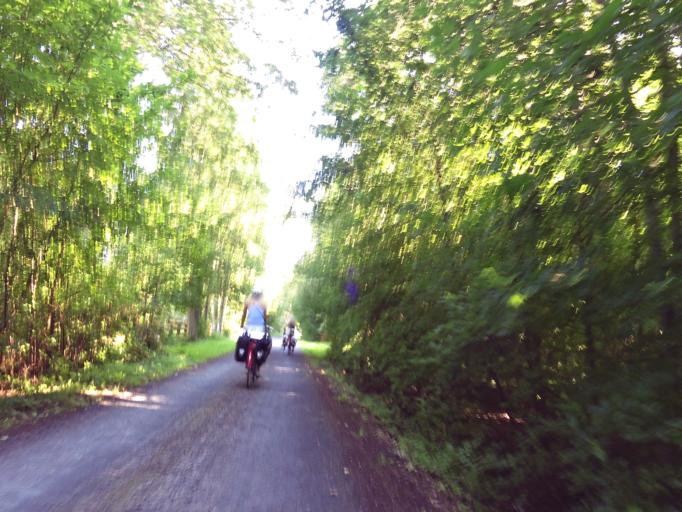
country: EE
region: Hiiumaa
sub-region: Kaerdla linn
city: Kardla
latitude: 58.7754
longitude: 22.4845
